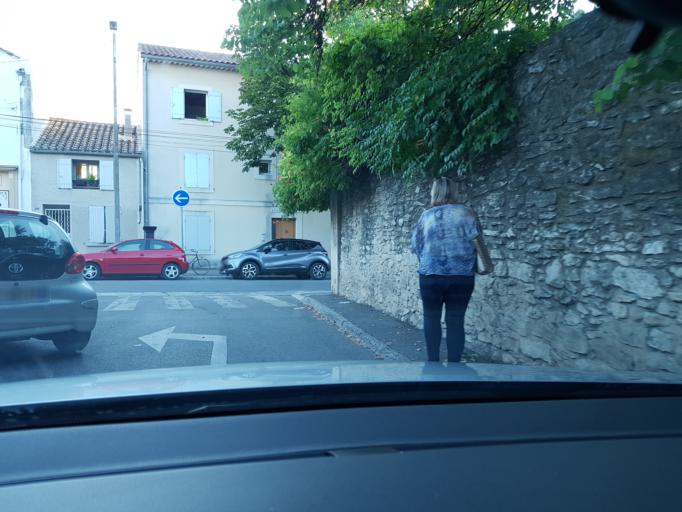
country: FR
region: Provence-Alpes-Cote d'Azur
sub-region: Departement des Bouches-du-Rhone
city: Saint-Remy-de-Provence
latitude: 43.7865
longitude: 4.8313
